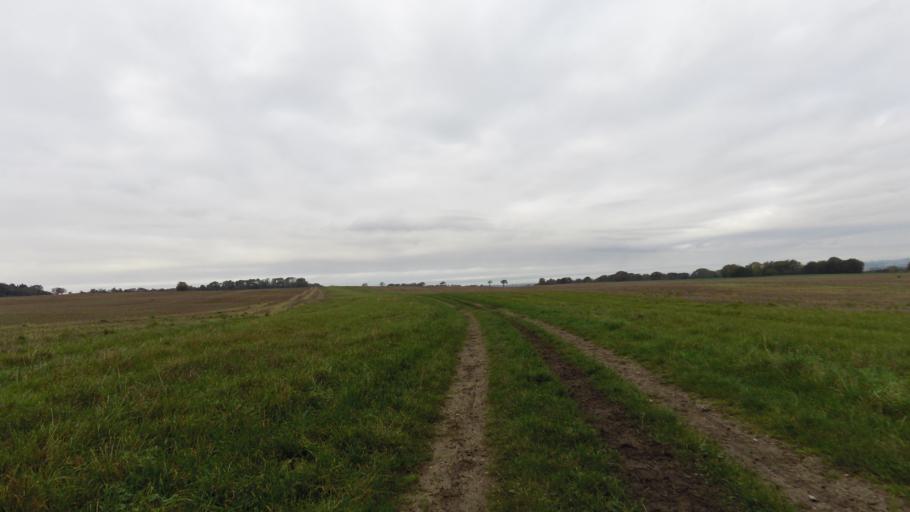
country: DK
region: Central Jutland
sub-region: Arhus Kommune
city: Kolt
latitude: 56.1327
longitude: 10.0867
